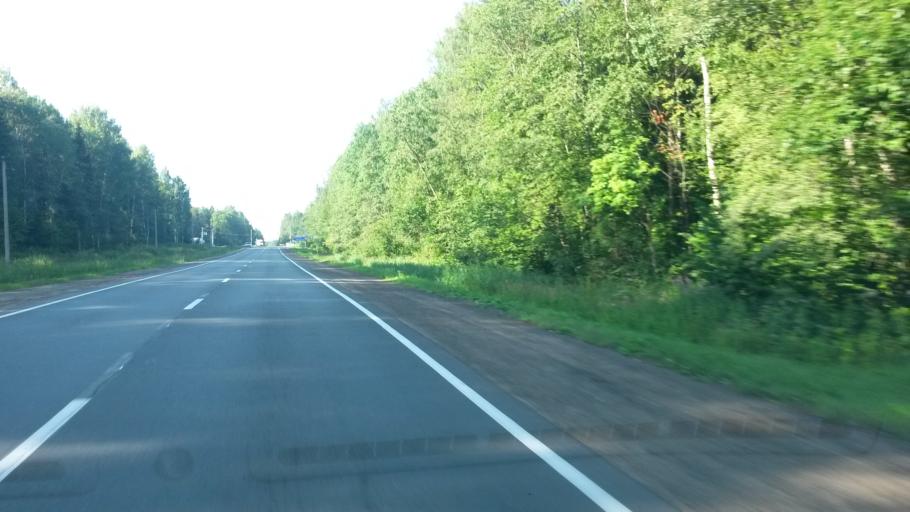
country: RU
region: Jaroslavl
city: Gavrilov-Yam
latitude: 57.2756
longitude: 39.9507
